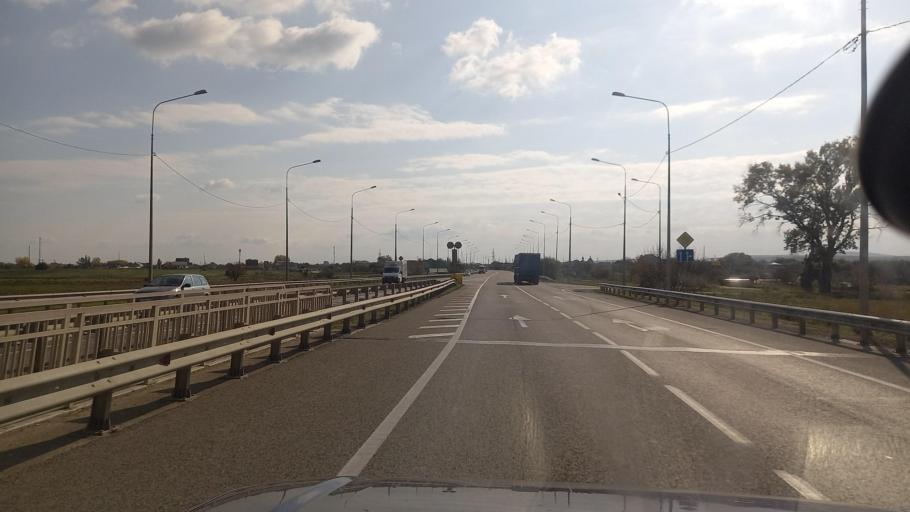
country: RU
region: Krasnodarskiy
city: Novoukrainskiy
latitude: 44.9007
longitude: 38.0379
